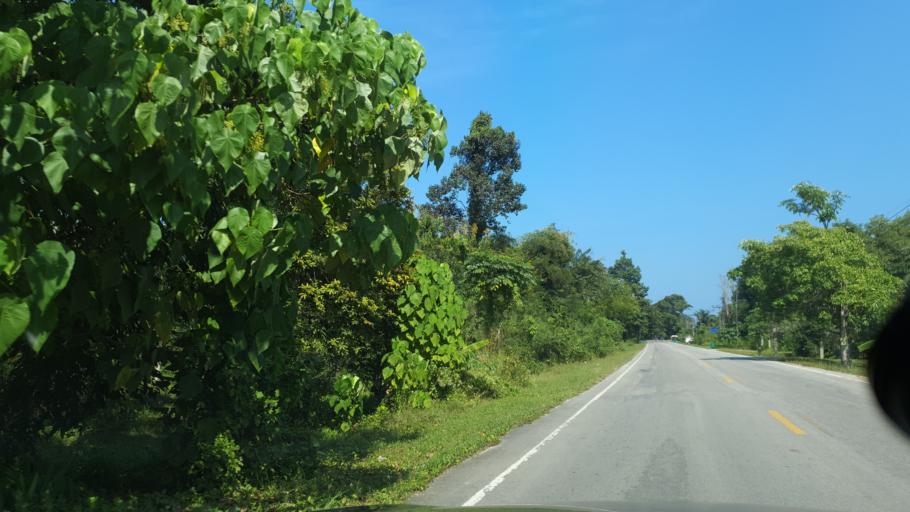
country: TH
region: Surat Thani
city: Tha Chana
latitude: 9.5751
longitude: 99.1825
